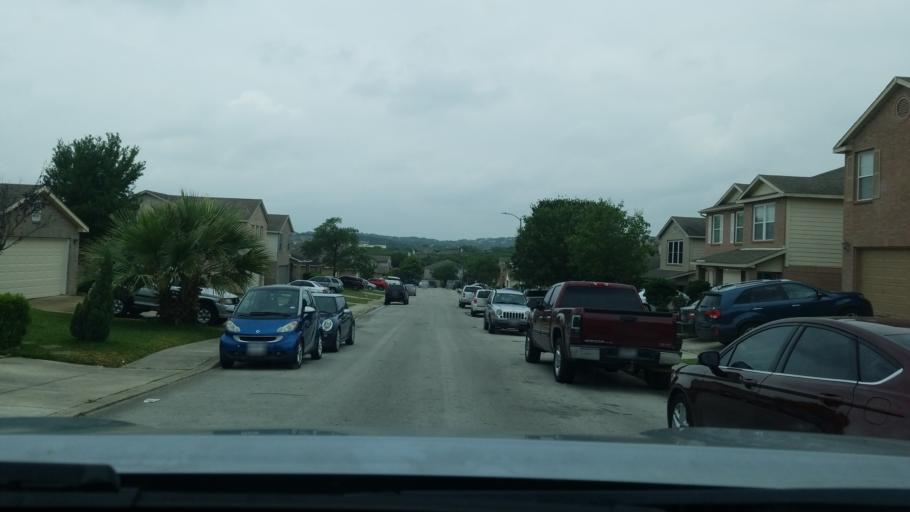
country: US
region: Texas
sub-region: Bexar County
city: Timberwood Park
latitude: 29.6826
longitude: -98.4637
